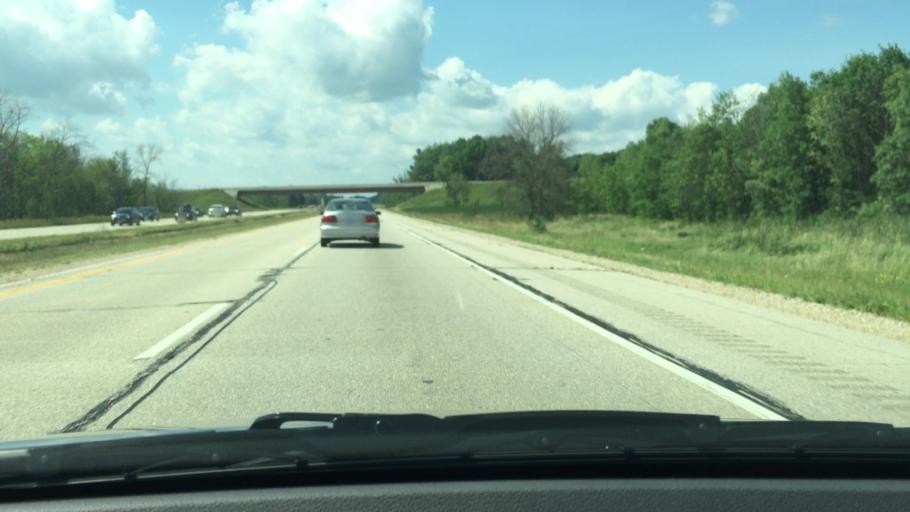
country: US
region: Wisconsin
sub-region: Washington County
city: Slinger
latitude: 43.4404
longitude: -88.3477
